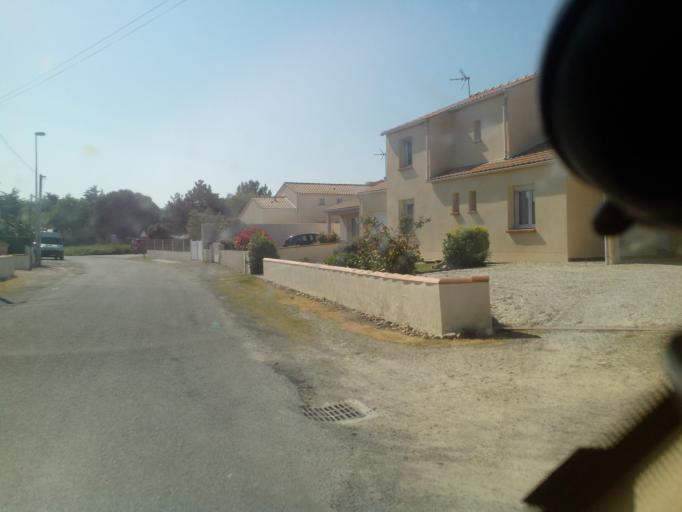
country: FR
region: Pays de la Loire
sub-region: Departement de la Loire-Atlantique
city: Pornic
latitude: 47.1019
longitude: -2.0631
